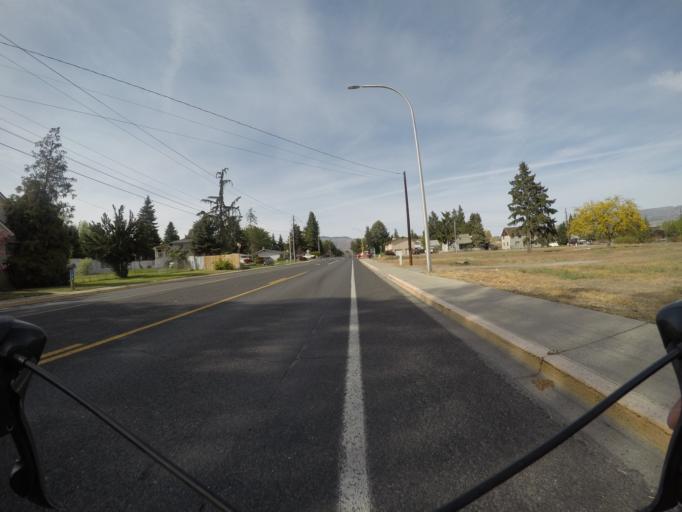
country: US
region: Washington
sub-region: Chelan County
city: West Wenatchee
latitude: 47.4256
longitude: -120.3460
